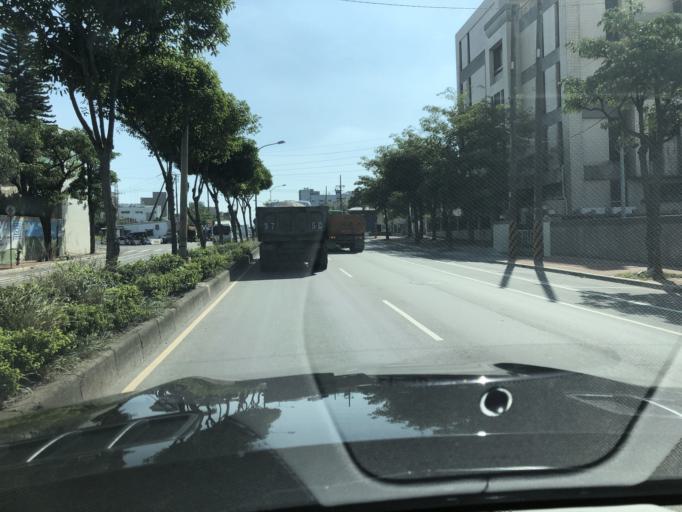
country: TW
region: Taiwan
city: Taoyuan City
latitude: 25.0765
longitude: 121.2854
